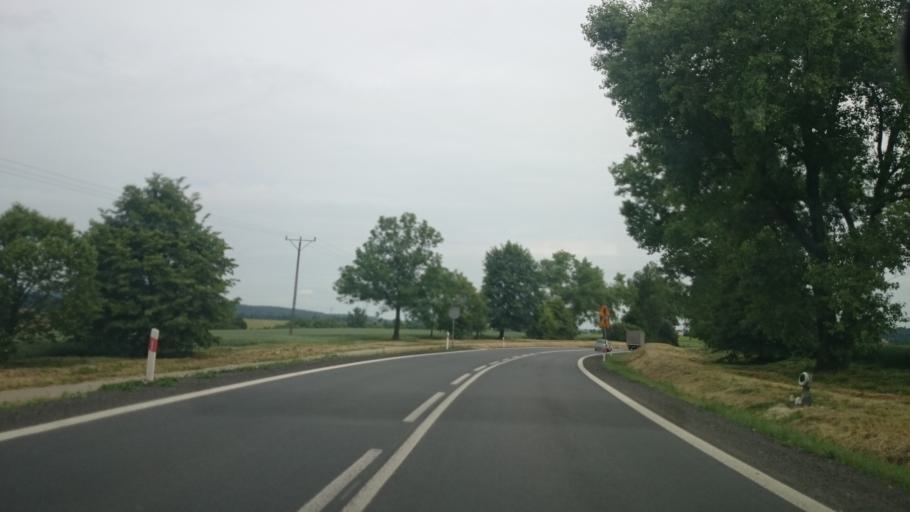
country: PL
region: Lower Silesian Voivodeship
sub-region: Powiat dzierzoniowski
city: Niemcza
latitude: 50.7017
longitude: 16.8231
